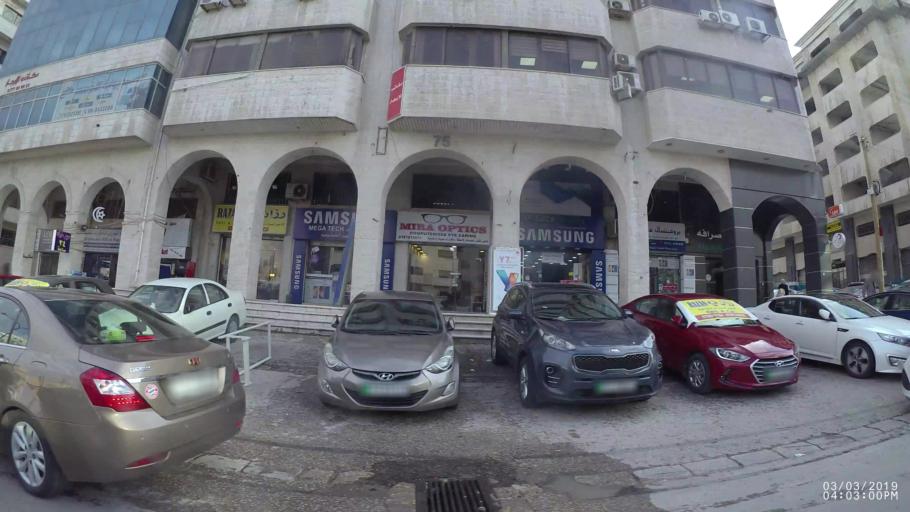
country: JO
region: Amman
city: Al Jubayhah
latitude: 31.9855
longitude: 35.8821
